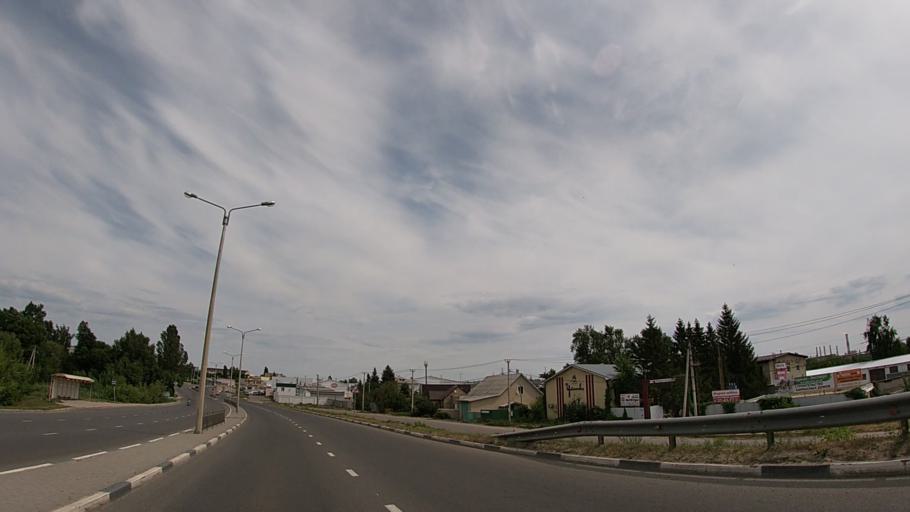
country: RU
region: Belgorod
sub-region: Belgorodskiy Rayon
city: Belgorod
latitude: 50.6088
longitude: 36.5336
